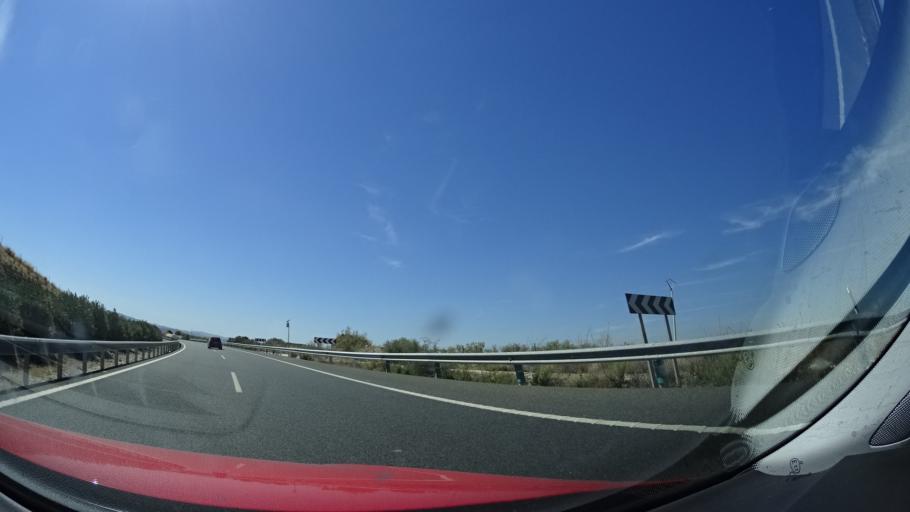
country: ES
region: Andalusia
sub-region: Provincia de Sevilla
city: Gilena
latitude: 37.2763
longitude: -4.9396
